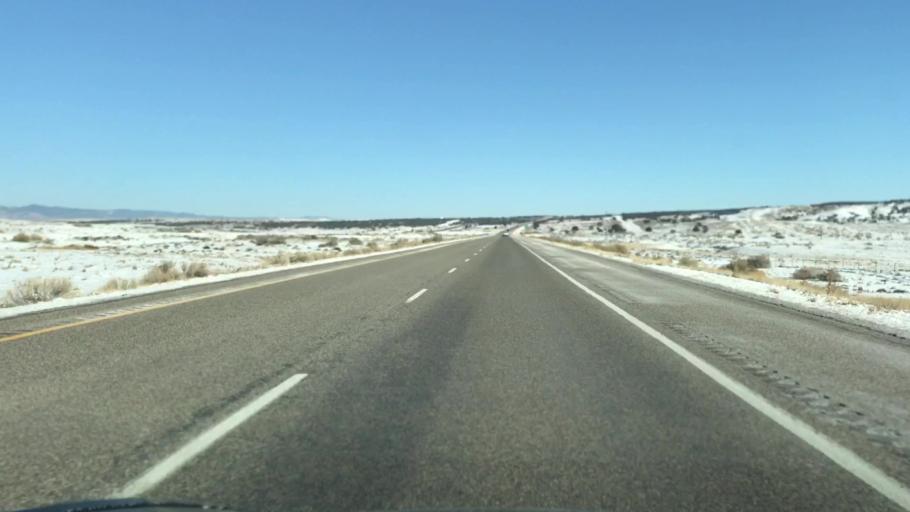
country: US
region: Colorado
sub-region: Mesa County
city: Loma
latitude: 39.1511
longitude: -109.1473
